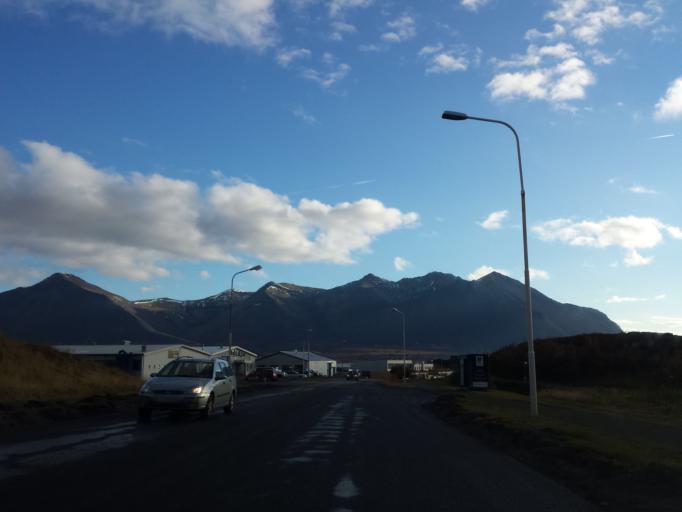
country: IS
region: West
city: Borgarnes
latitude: 64.5474
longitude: -21.9105
